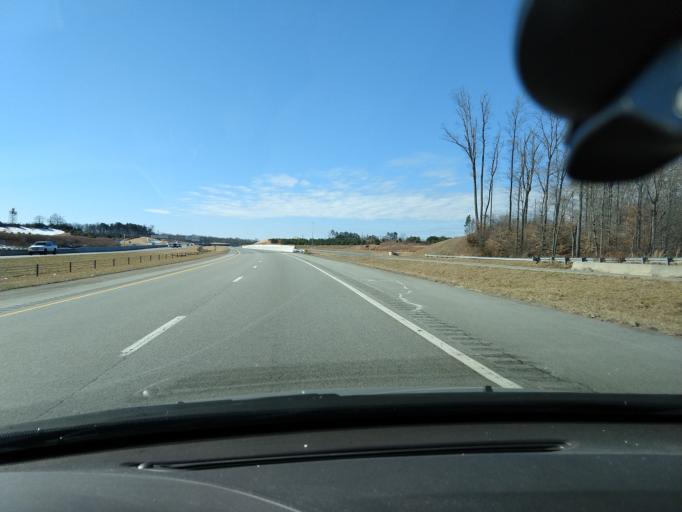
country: US
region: North Carolina
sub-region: Guilford County
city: Oak Ridge
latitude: 36.1228
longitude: -79.9359
